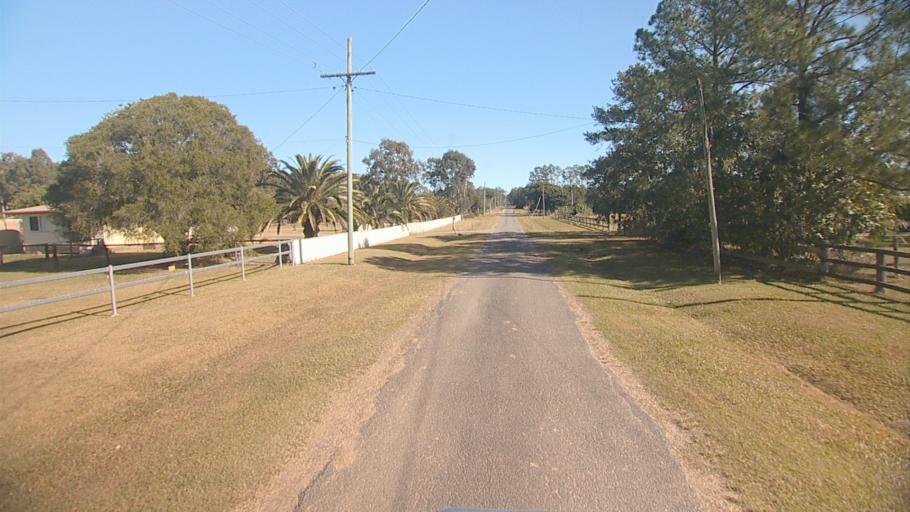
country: AU
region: Queensland
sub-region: Logan
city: Chambers Flat
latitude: -27.7578
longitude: 153.0798
